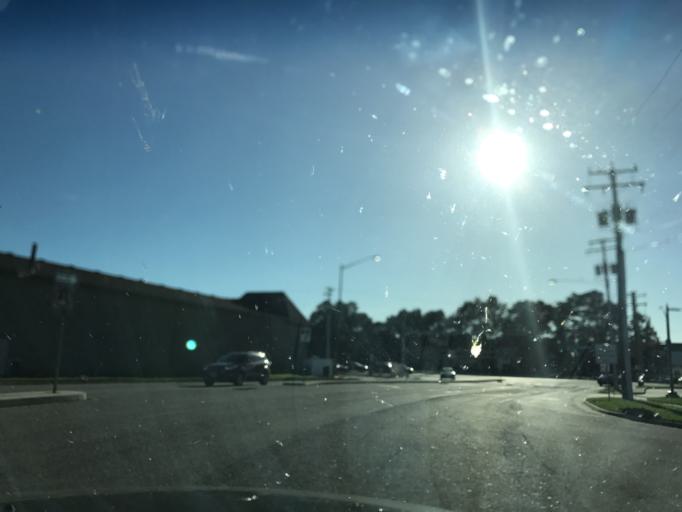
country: US
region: Virginia
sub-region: City of Chesapeake
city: Chesapeake
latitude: 36.7687
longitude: -76.2509
